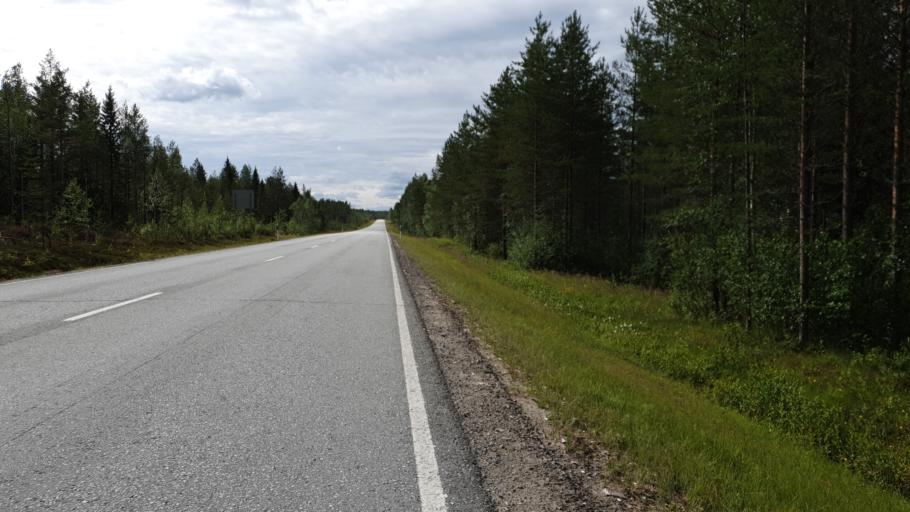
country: FI
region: Kainuu
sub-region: Kehys-Kainuu
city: Kuhmo
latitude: 64.5292
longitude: 29.9449
